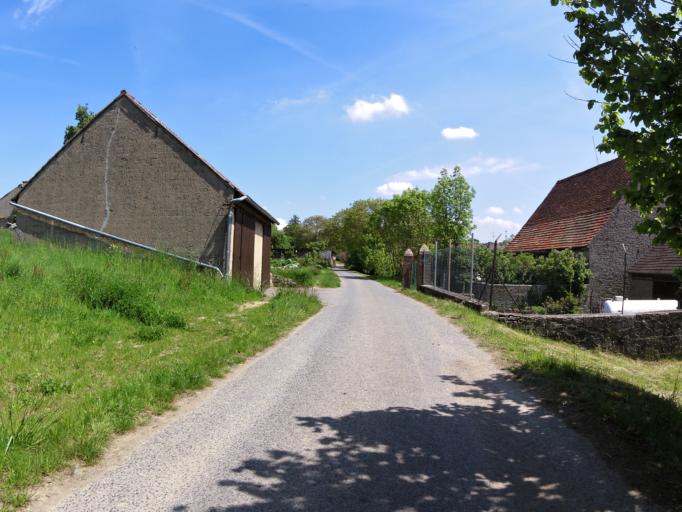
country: DE
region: Bavaria
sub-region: Regierungsbezirk Unterfranken
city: Theilheim
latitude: 49.7336
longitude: 10.0345
